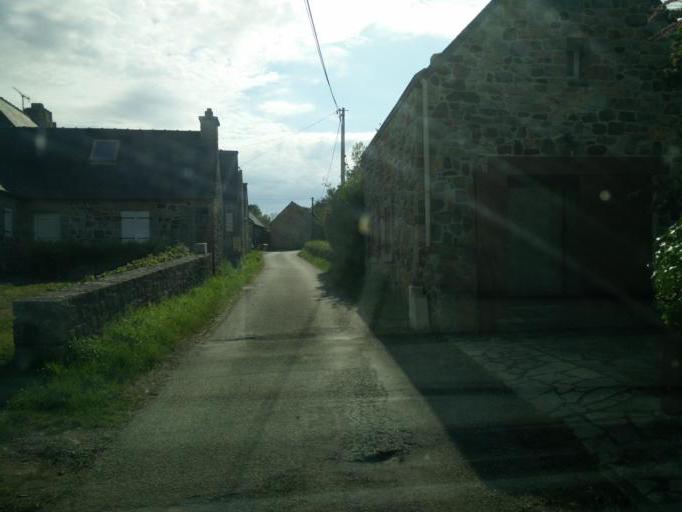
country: FR
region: Brittany
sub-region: Departement du Finistere
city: Crozon
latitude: 48.2345
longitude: -4.5477
